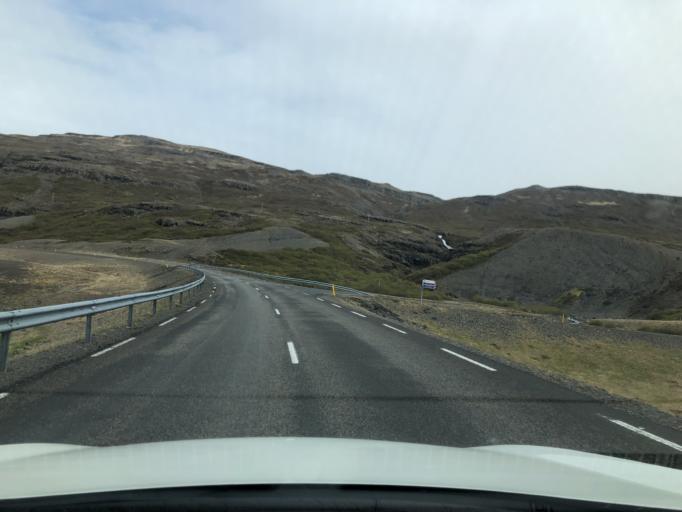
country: IS
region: Capital Region
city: Mosfellsbaer
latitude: 64.3849
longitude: -21.3547
